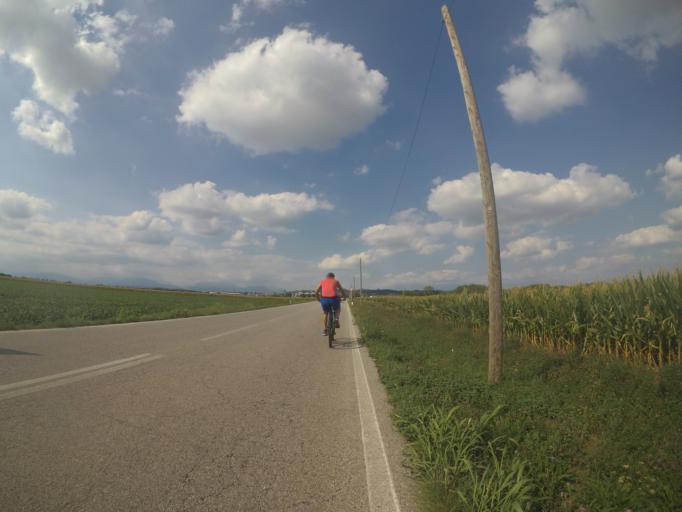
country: IT
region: Friuli Venezia Giulia
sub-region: Provincia di Udine
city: Fagagna
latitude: 46.0890
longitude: 13.0903
